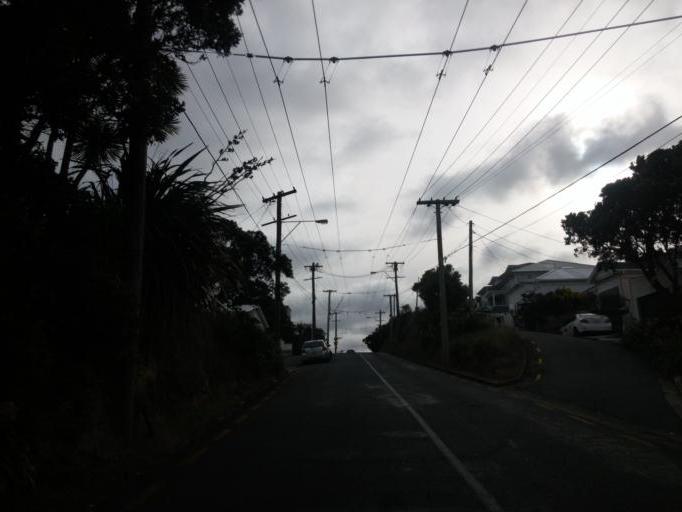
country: NZ
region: Wellington
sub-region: Wellington City
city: Brooklyn
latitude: -41.3118
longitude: 174.7659
